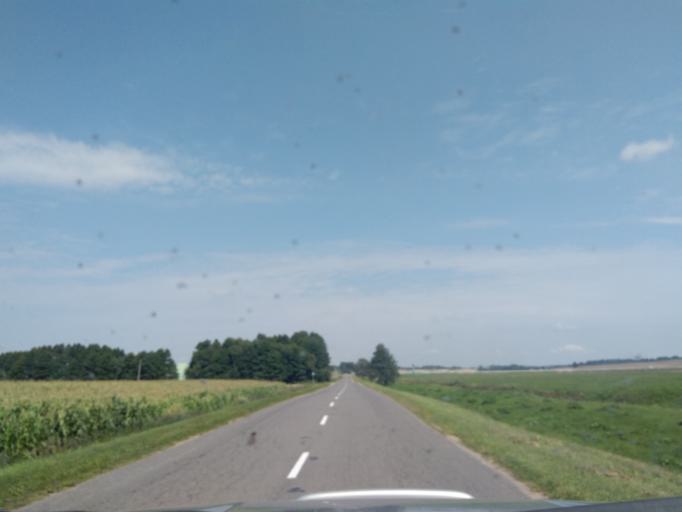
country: BY
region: Minsk
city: Valozhyn
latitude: 54.0327
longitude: 26.6046
